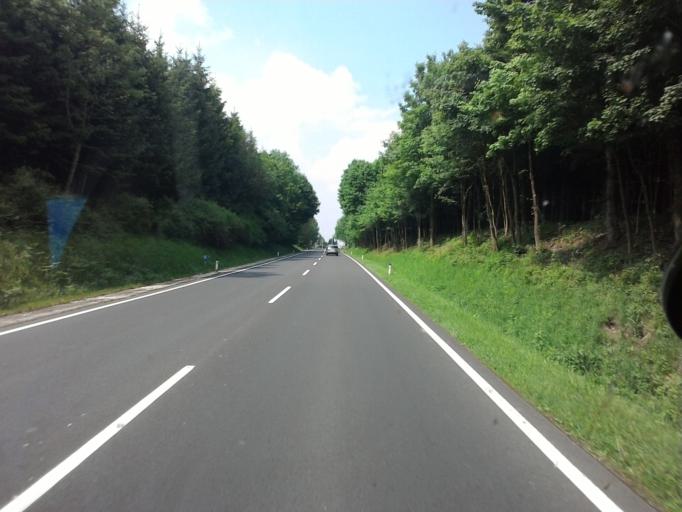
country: AT
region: Upper Austria
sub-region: Wels-Land
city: Steinhaus
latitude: 48.0986
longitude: 14.0408
